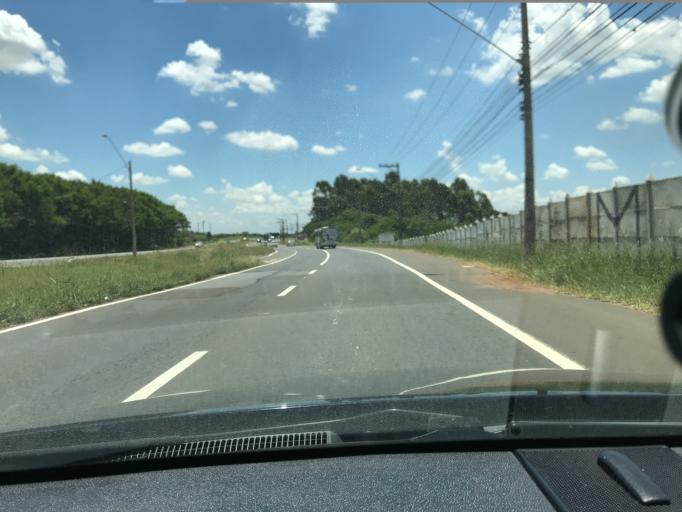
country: BR
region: Sao Paulo
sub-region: Campinas
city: Campinas
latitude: -22.8677
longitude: -47.0966
